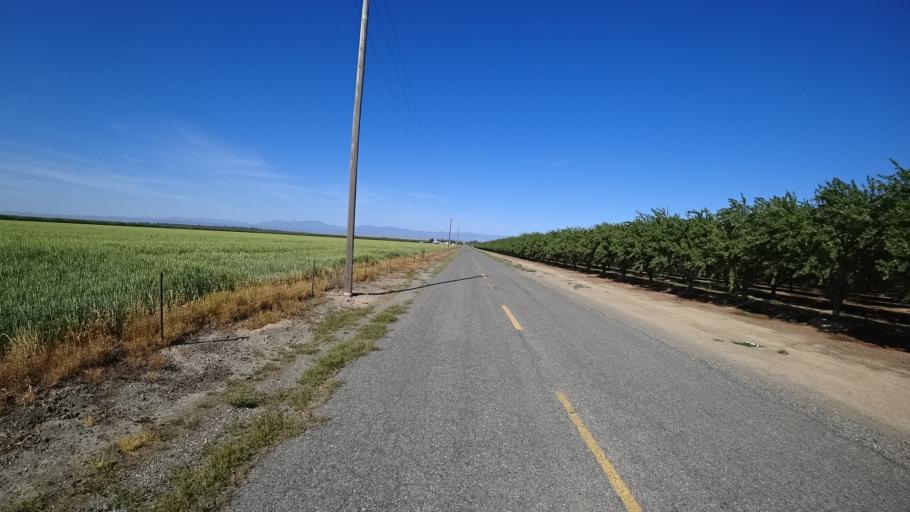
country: US
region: California
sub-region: Glenn County
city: Willows
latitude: 39.6112
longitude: -122.1608
